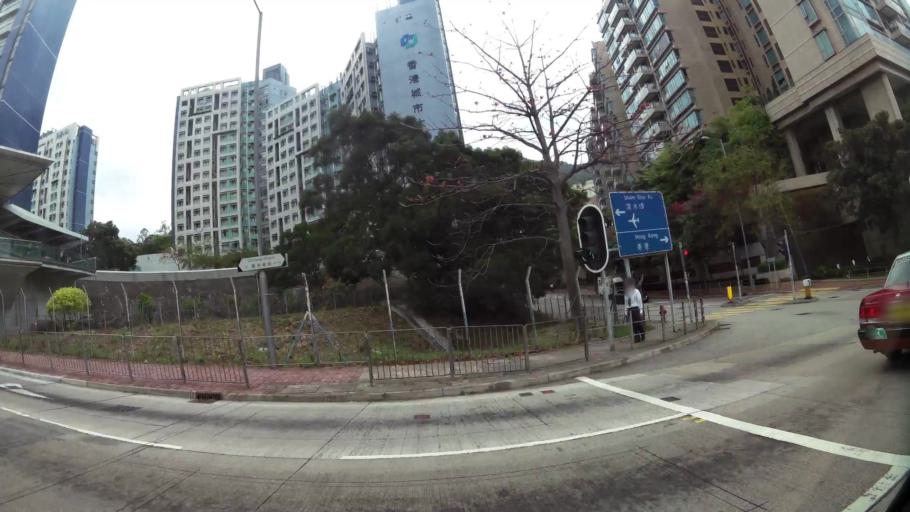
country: HK
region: Sham Shui Po
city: Sham Shui Po
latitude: 22.3396
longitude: 114.1717
